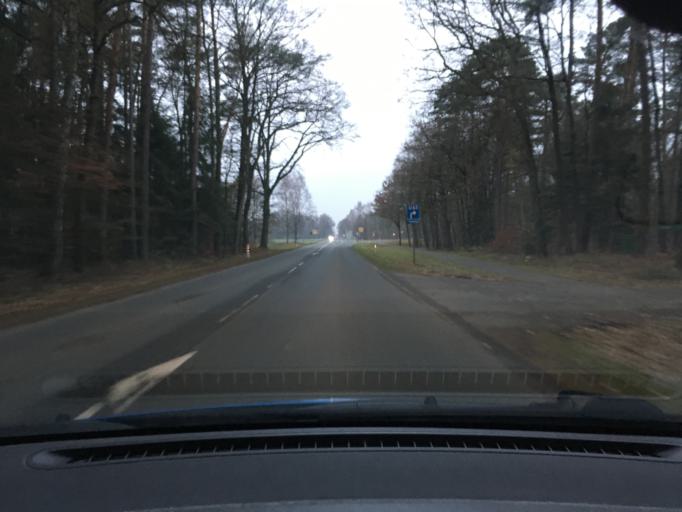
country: DE
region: Lower Saxony
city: Bispingen
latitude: 53.1195
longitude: 9.9518
